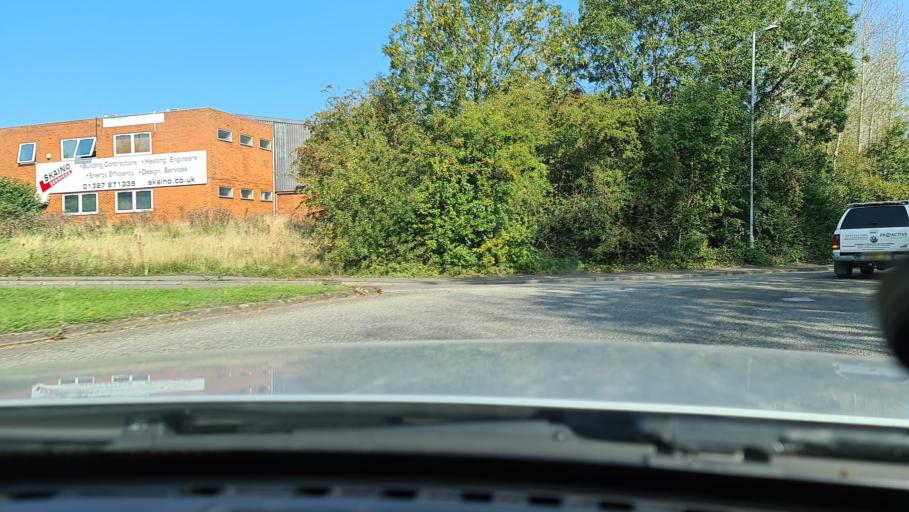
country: GB
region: England
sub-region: Northamptonshire
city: Daventry
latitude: 52.2471
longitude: -1.1518
